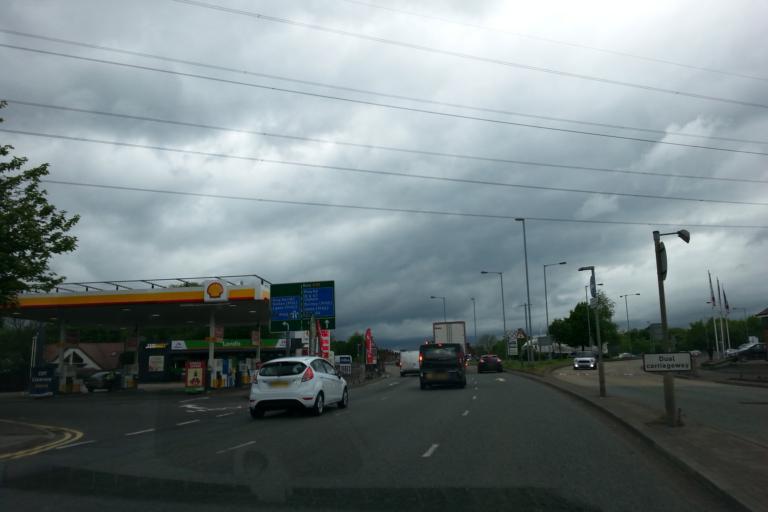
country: GB
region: England
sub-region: Borough of Bury
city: Prestwich
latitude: 53.5373
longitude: -2.2883
